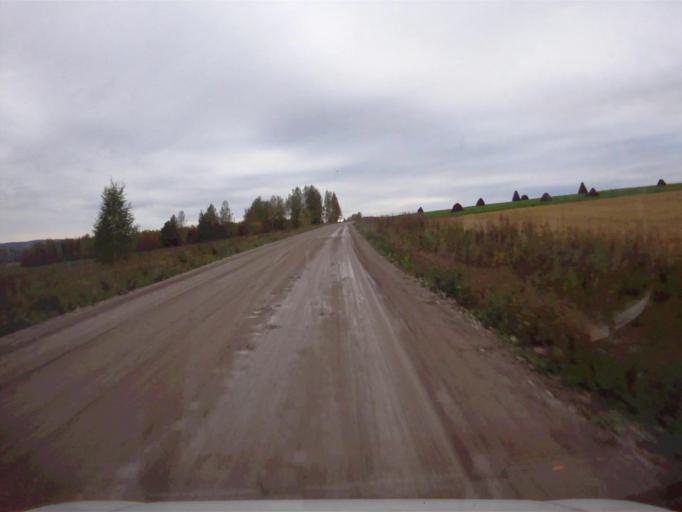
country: RU
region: Sverdlovsk
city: Mikhaylovsk
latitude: 56.1768
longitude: 59.2101
